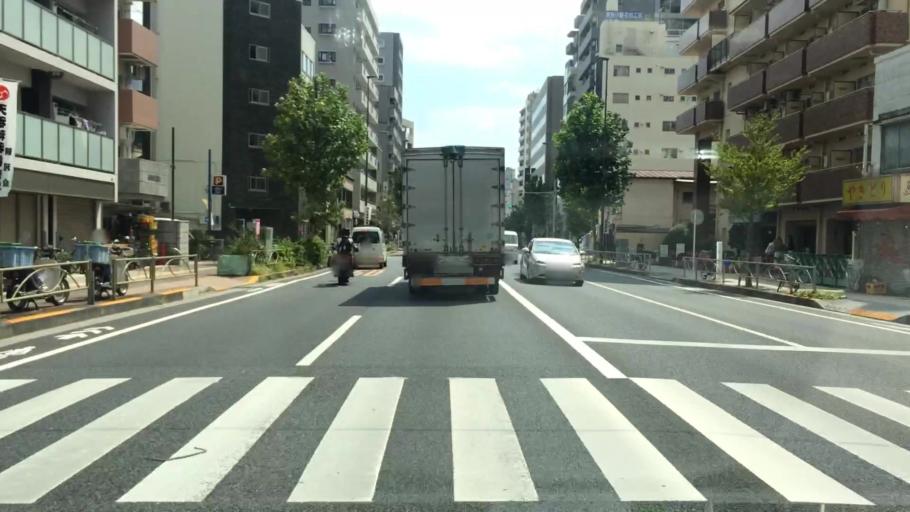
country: JP
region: Tokyo
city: Tokyo
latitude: 35.7276
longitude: 139.7272
